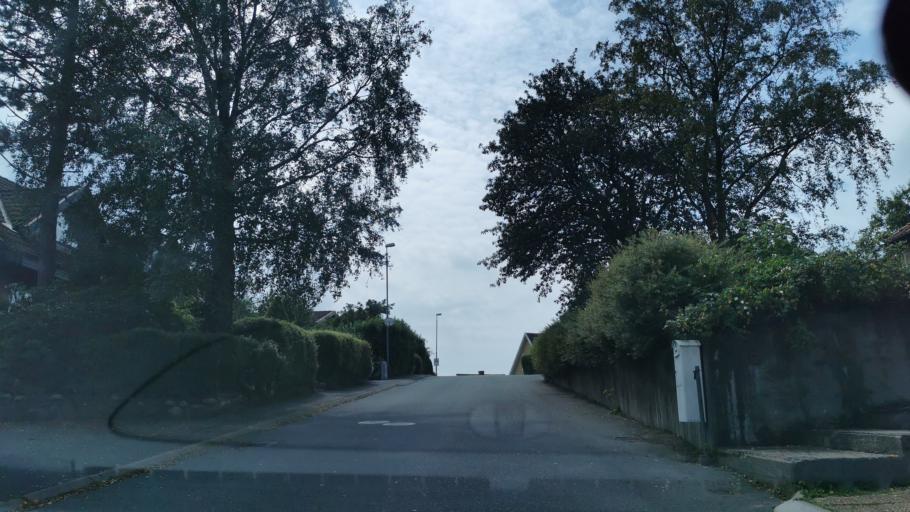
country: SE
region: Vaestra Goetaland
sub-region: Goteborg
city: Goeteborg
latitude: 57.6769
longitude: 11.9815
